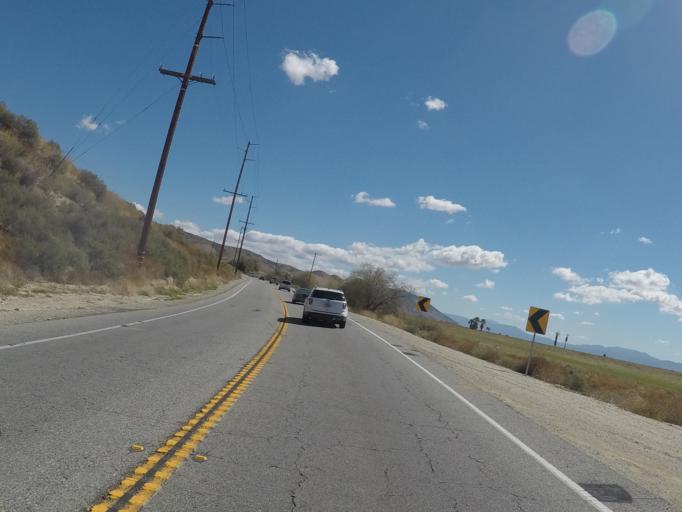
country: US
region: California
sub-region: Riverside County
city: Lakeview
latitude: 33.8908
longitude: -117.0769
